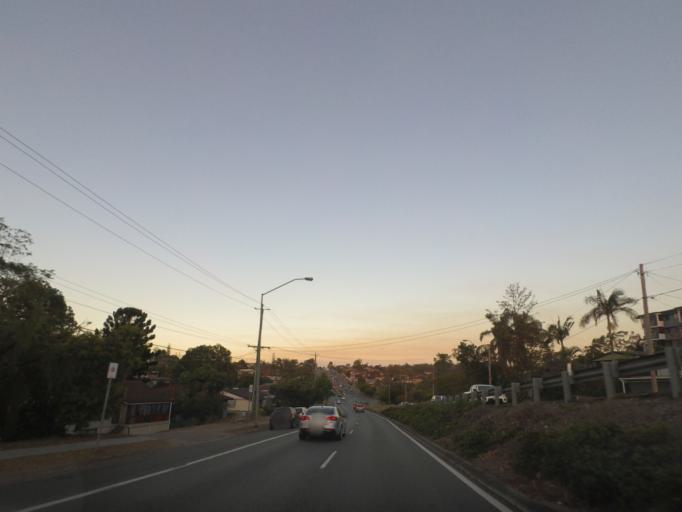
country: AU
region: Queensland
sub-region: Brisbane
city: Upper Mount Gravatt
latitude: -27.5577
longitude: 153.0865
